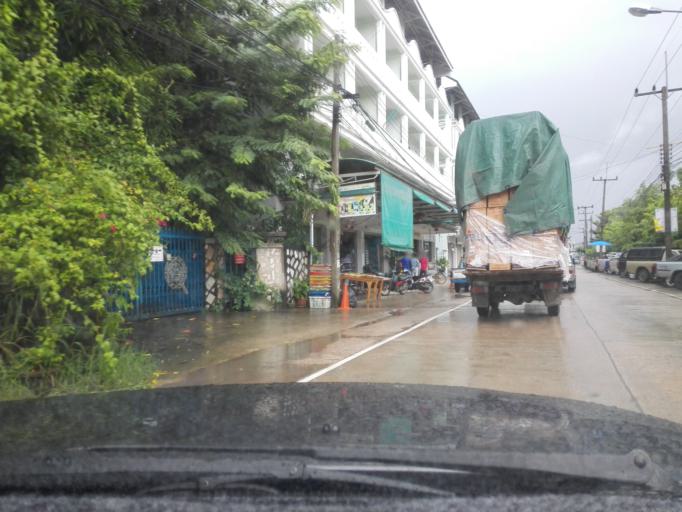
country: TH
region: Tak
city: Mae Sot
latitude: 16.7096
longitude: 98.5717
